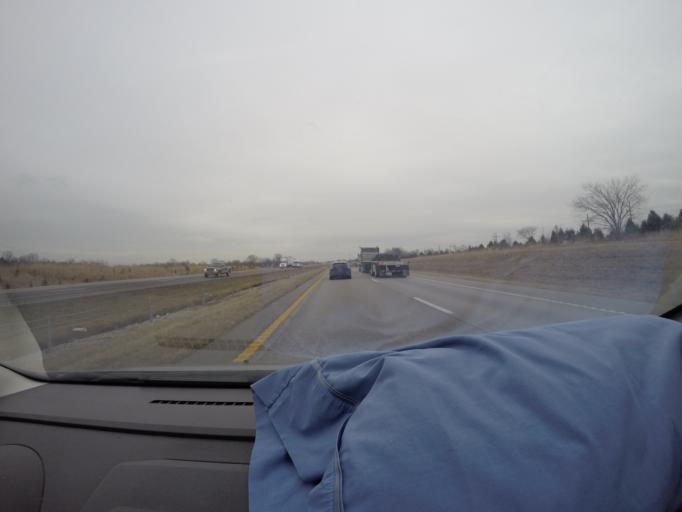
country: US
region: Missouri
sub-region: Warren County
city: Wright City
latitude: 38.8209
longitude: -90.9793
